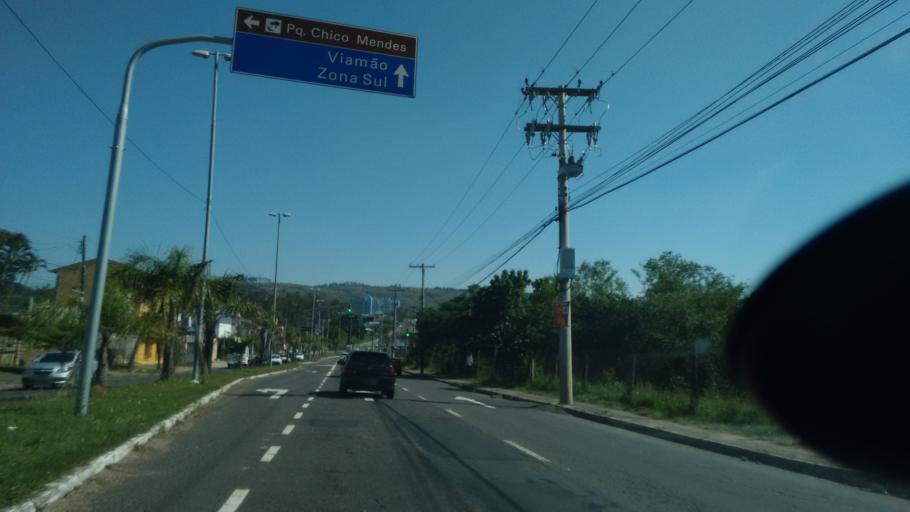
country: BR
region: Rio Grande do Sul
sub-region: Cachoeirinha
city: Cachoeirinha
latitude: -30.0249
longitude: -51.1201
